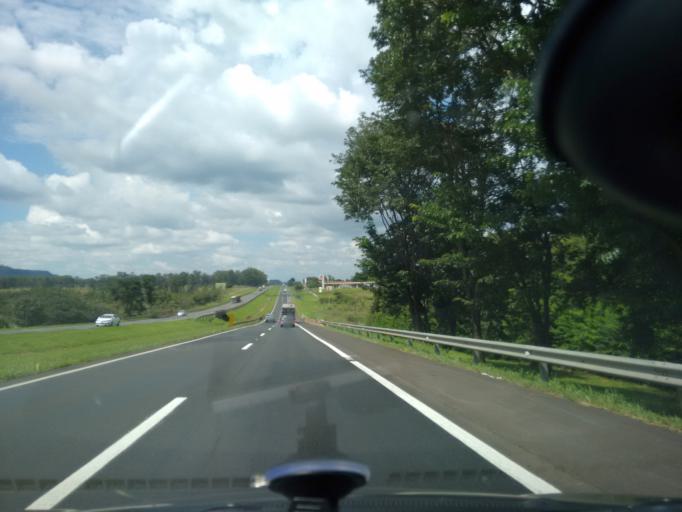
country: BR
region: Sao Paulo
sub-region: Sao Carlos
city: Sao Carlos
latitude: -22.0864
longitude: -47.8354
